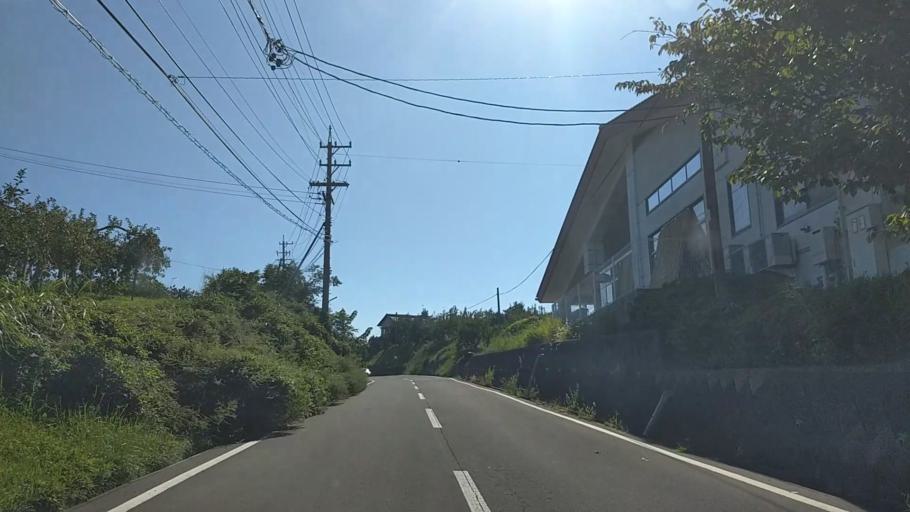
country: JP
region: Nagano
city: Nagano-shi
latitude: 36.5793
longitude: 138.1197
